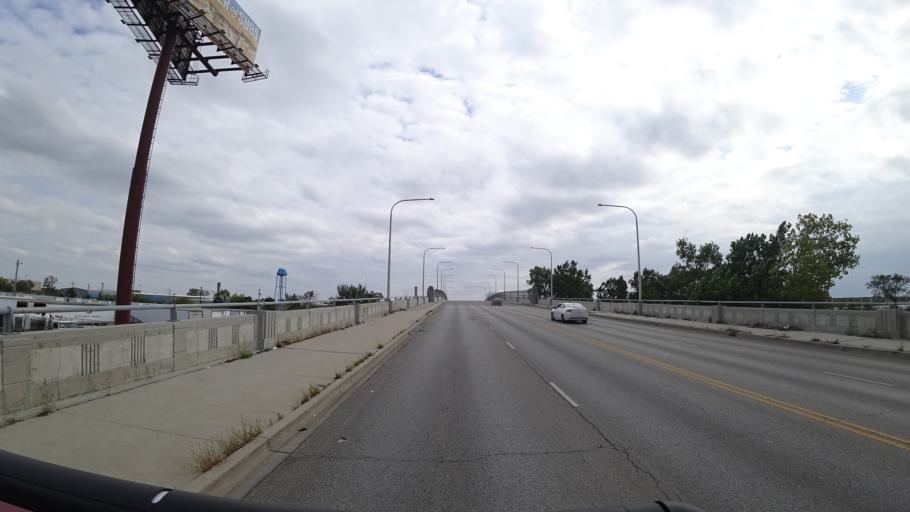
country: US
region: Illinois
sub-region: Cook County
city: Cicero
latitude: 41.8699
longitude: -87.7546
